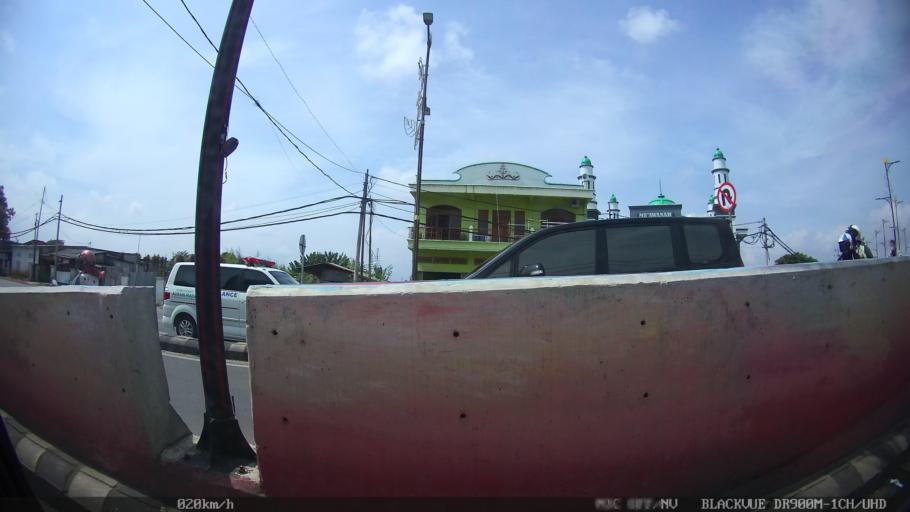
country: ID
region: Lampung
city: Kedaton
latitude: -5.3789
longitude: 105.2604
